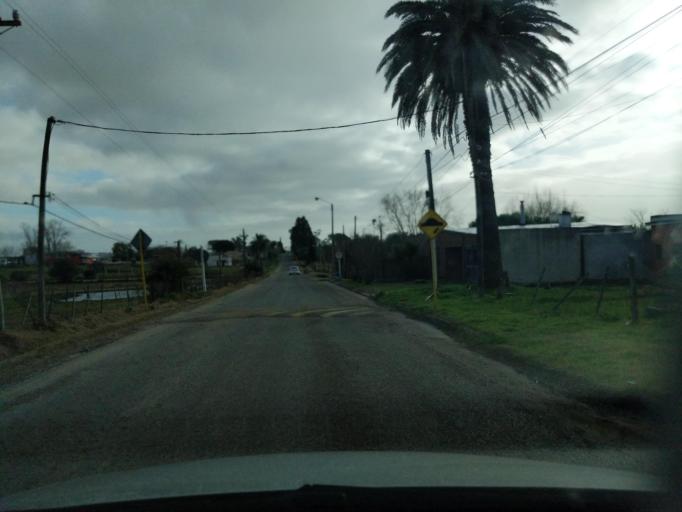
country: UY
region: Florida
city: Florida
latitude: -34.0810
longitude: -56.2119
